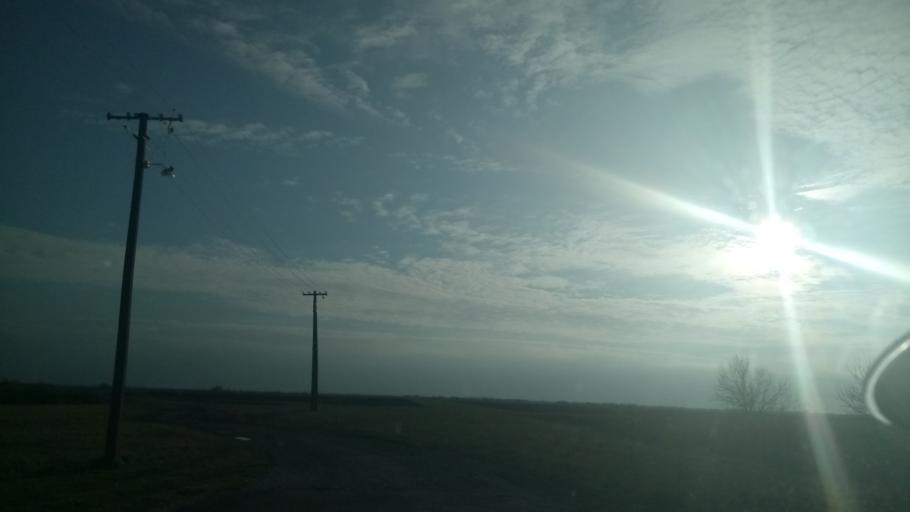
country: RS
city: Vojka
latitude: 44.9360
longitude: 20.1290
